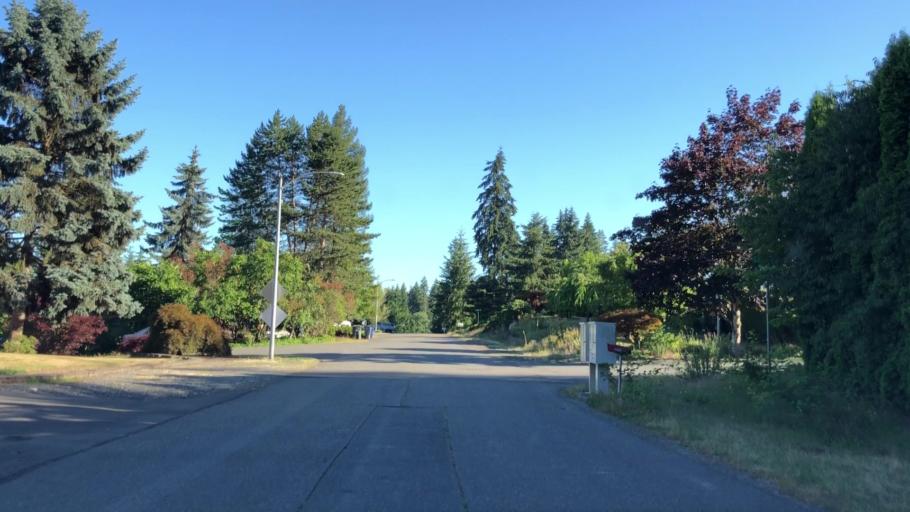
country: US
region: Washington
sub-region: King County
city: Bothell
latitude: 47.7954
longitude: -122.2276
